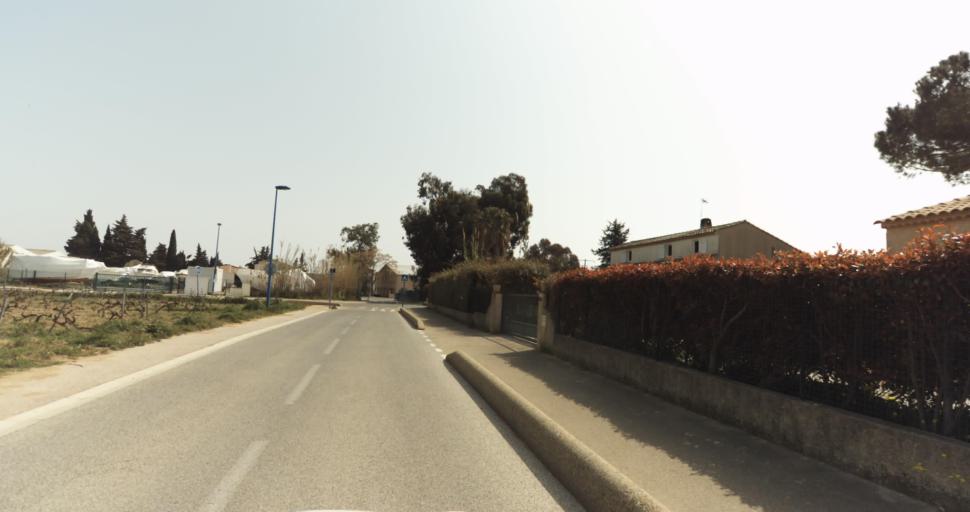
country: FR
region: Provence-Alpes-Cote d'Azur
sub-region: Departement du Var
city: Bormes-les-Mimosas
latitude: 43.1327
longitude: 6.3458
